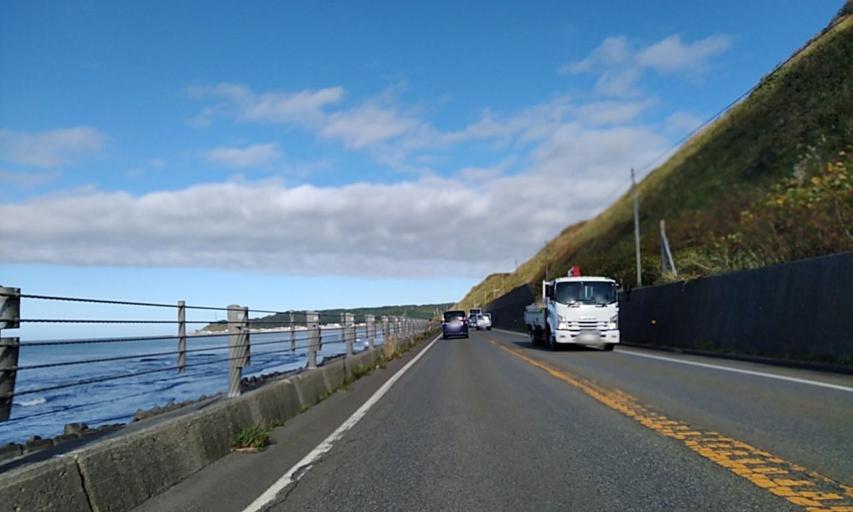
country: JP
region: Hokkaido
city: Shizunai-furukawacho
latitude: 42.2617
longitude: 142.5195
